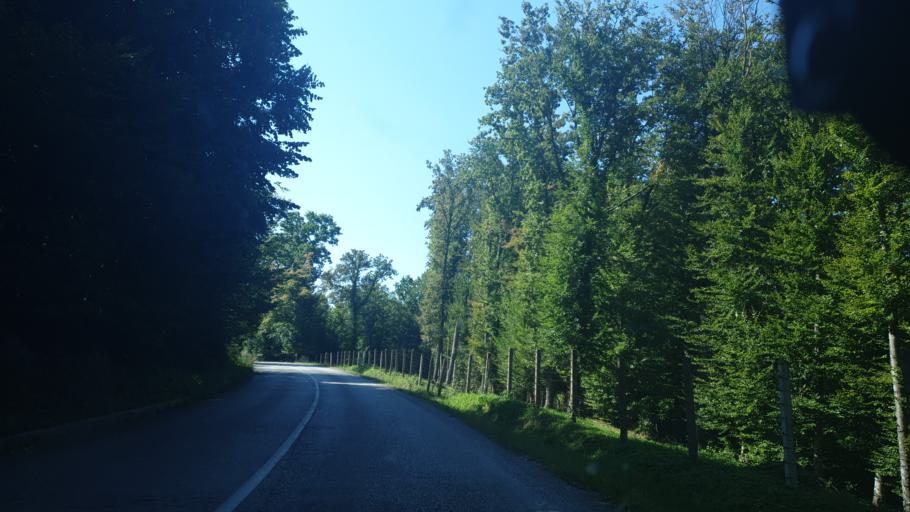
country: RS
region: Central Serbia
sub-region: Kolubarski Okrug
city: Lajkovac
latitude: 44.3175
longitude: 20.1818
